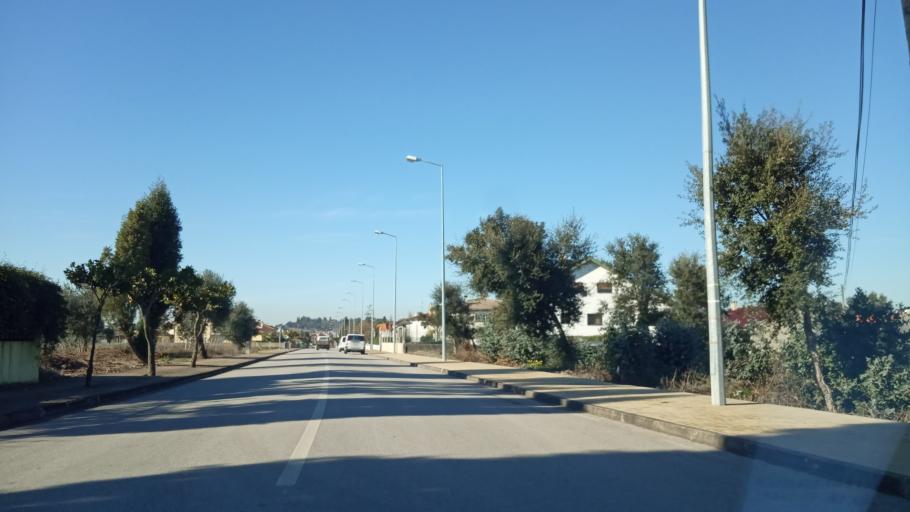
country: PT
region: Aveiro
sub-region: Anadia
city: Anadia
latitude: 40.4331
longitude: -8.4265
